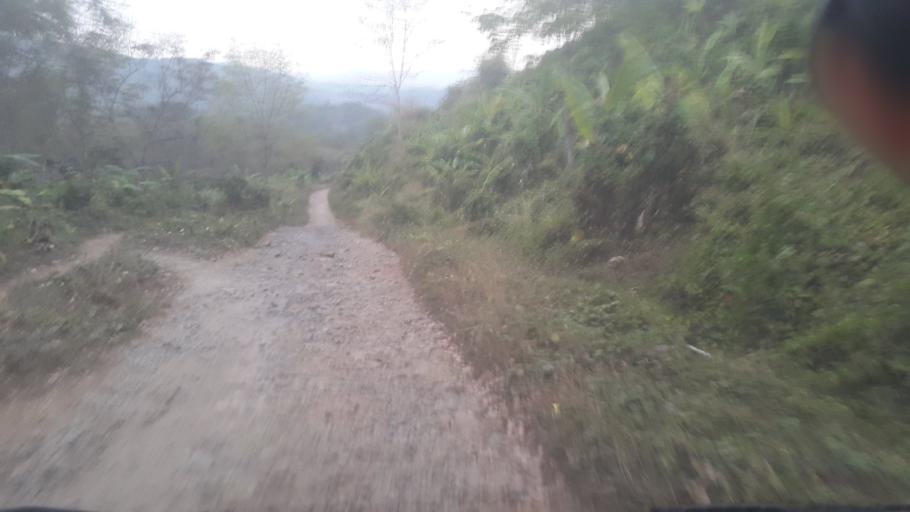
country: ID
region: West Java
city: Citarik
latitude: -6.9743
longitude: 106.6010
